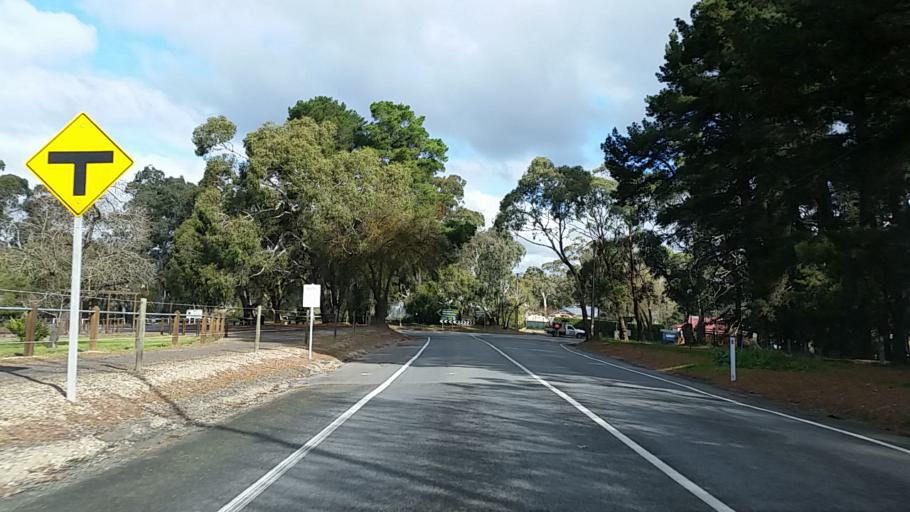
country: AU
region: South Australia
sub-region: Mount Barker
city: Hahndorf
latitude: -35.0980
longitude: 138.7917
